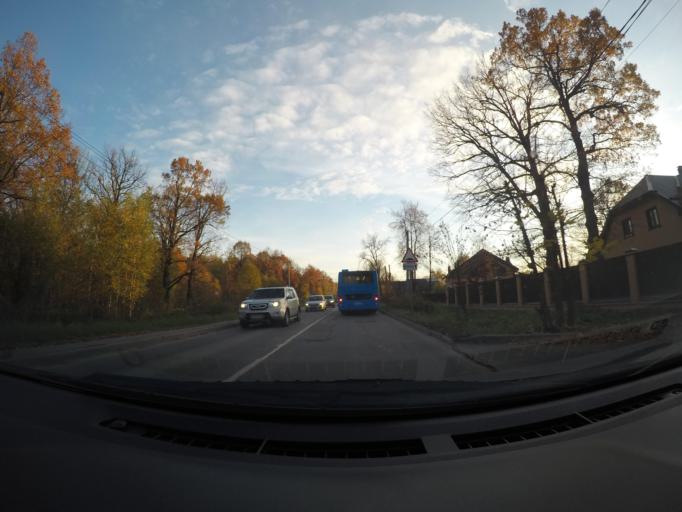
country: RU
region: Moskovskaya
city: Firsanovka
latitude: 55.9452
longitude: 37.2506
